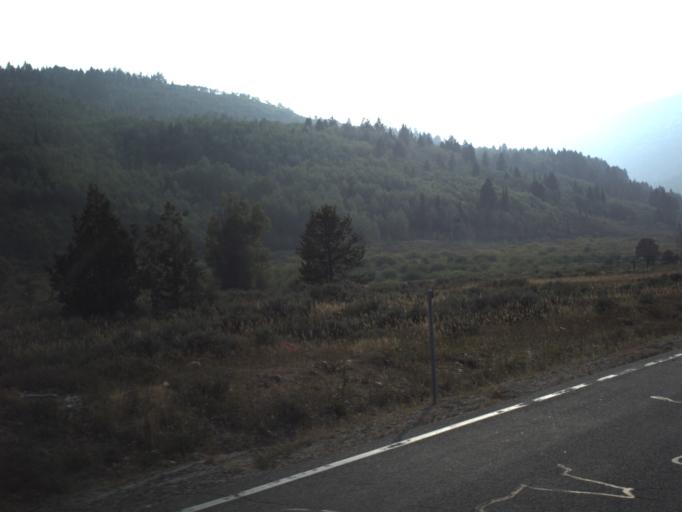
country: US
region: Utah
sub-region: Summit County
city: Kamas
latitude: 40.6304
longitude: -111.1806
